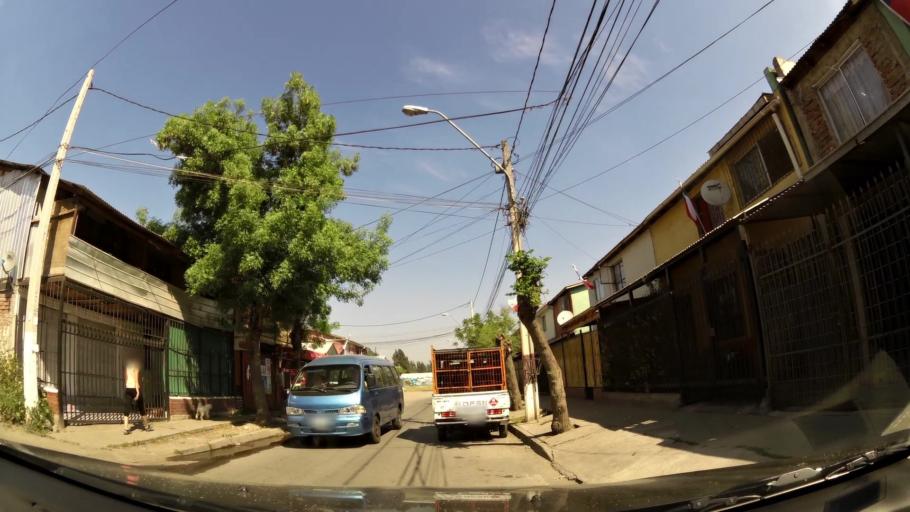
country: CL
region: Santiago Metropolitan
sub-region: Provincia de Cordillera
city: Puente Alto
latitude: -33.6321
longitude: -70.6163
